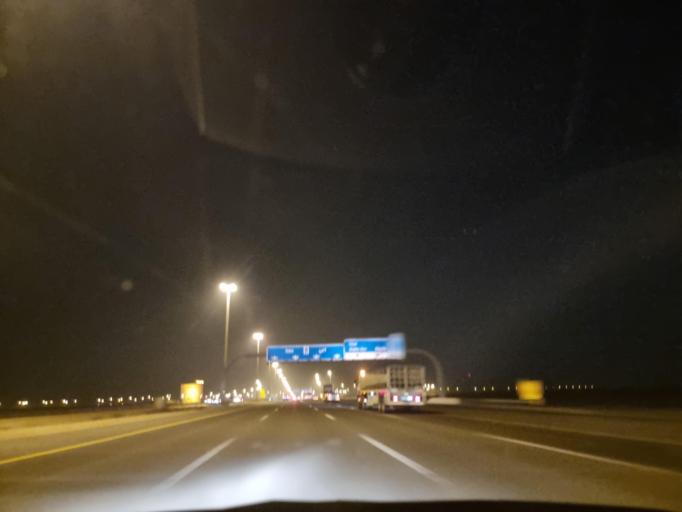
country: AE
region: Abu Dhabi
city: Abu Dhabi
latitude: 24.6619
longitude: 54.8039
